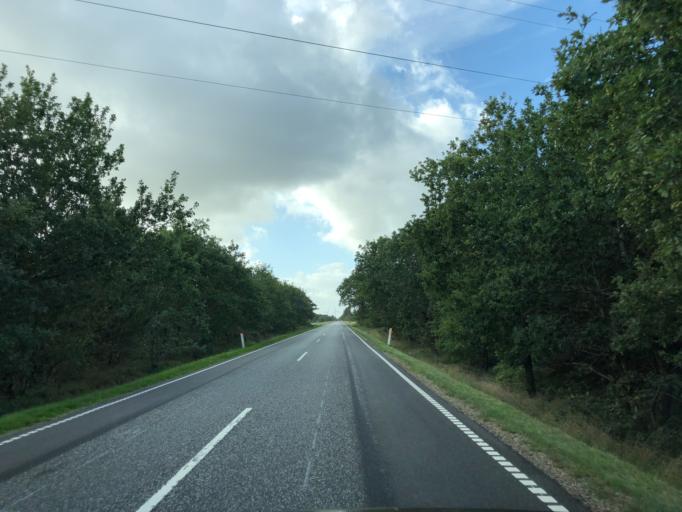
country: DK
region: Central Jutland
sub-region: Holstebro Kommune
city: Holstebro
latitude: 56.3706
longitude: 8.5459
